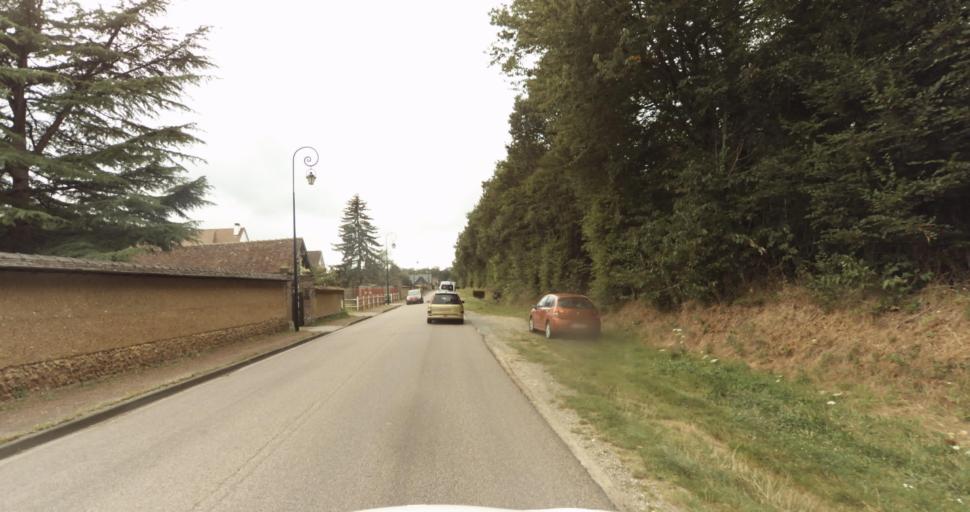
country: FR
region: Haute-Normandie
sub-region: Departement de l'Eure
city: Arnieres-sur-Iton
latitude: 48.9717
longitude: 1.0918
